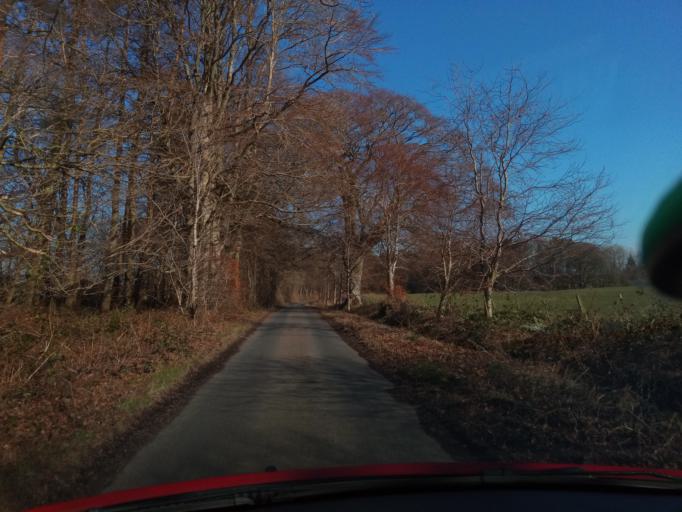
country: GB
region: Scotland
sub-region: The Scottish Borders
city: Hawick
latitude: 55.5041
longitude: -2.7656
